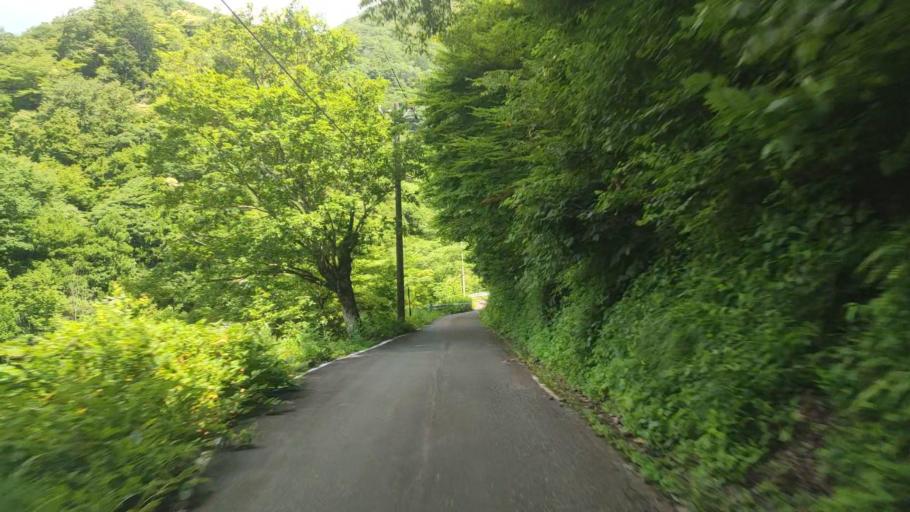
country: JP
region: Fukui
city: Ono
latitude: 35.7448
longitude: 136.5830
